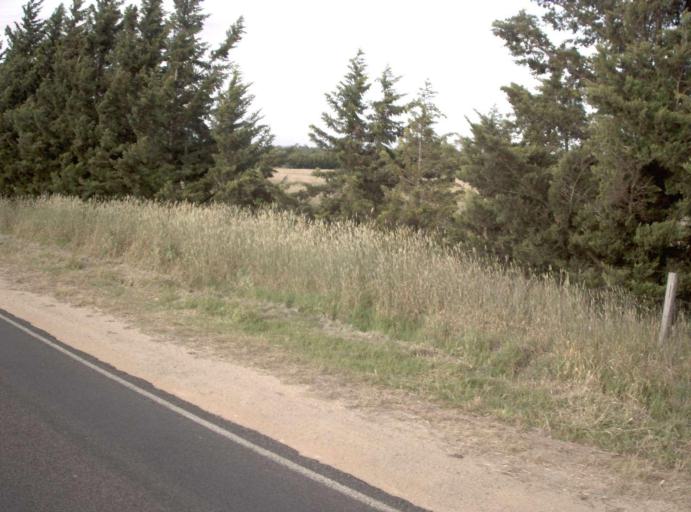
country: AU
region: Victoria
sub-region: Wellington
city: Heyfield
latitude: -37.9968
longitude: 146.7779
